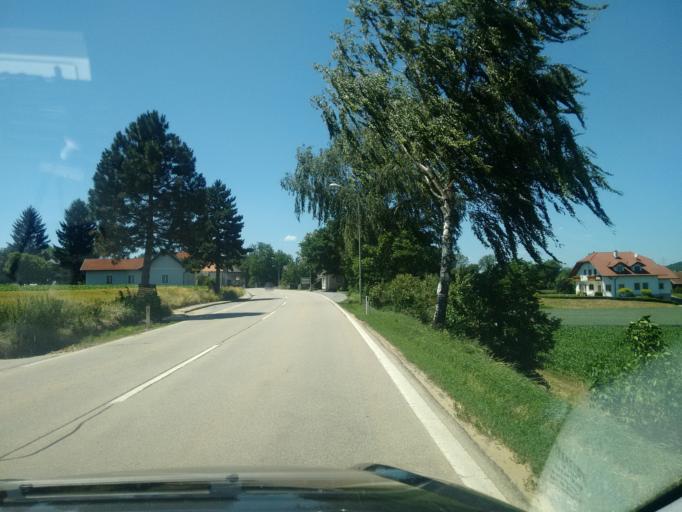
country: AT
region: Lower Austria
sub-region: Politischer Bezirk Sankt Polten
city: Kapelln
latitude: 48.2624
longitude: 15.7742
